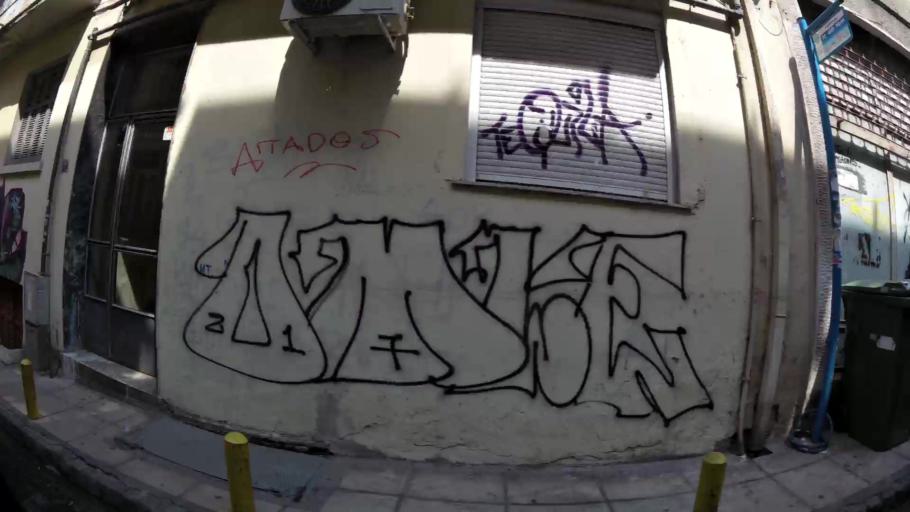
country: GR
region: Central Macedonia
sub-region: Nomos Thessalonikis
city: Sykies
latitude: 40.6417
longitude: 22.9449
